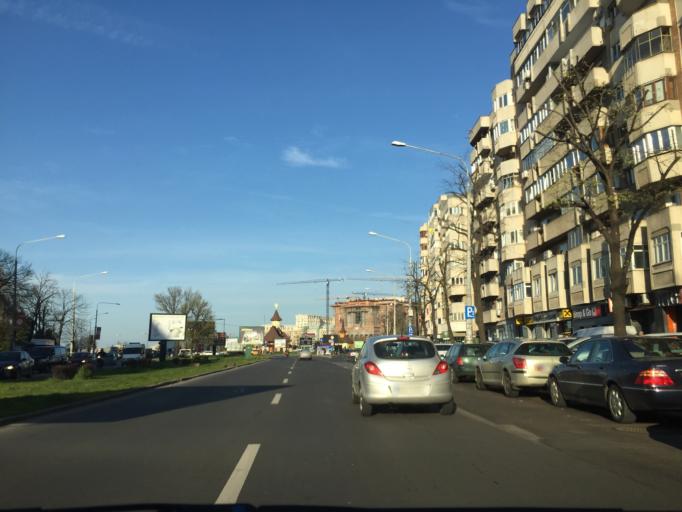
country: RO
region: Bucuresti
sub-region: Municipiul Bucuresti
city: Bucuresti
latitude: 44.4243
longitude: 26.0758
